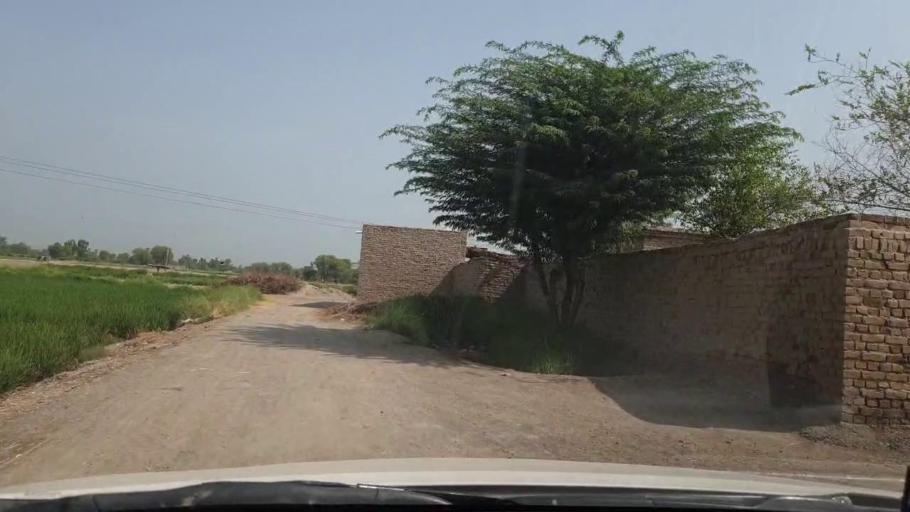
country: PK
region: Sindh
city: Shikarpur
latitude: 27.9749
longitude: 68.6705
